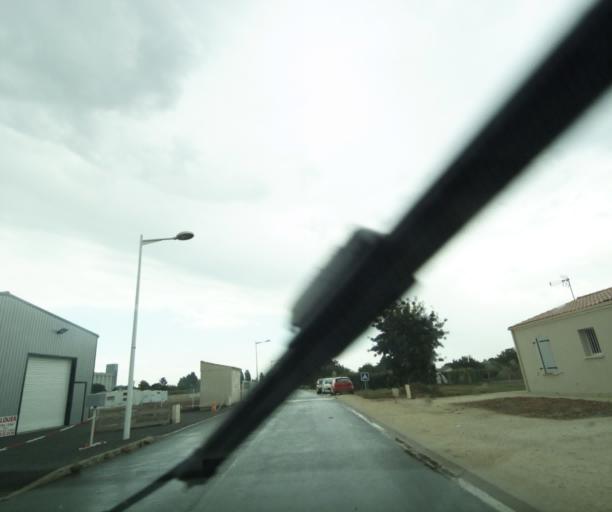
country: FR
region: Poitou-Charentes
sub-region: Departement de la Charente-Maritime
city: Tonnay-Charente
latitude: 45.9519
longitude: -0.8808
